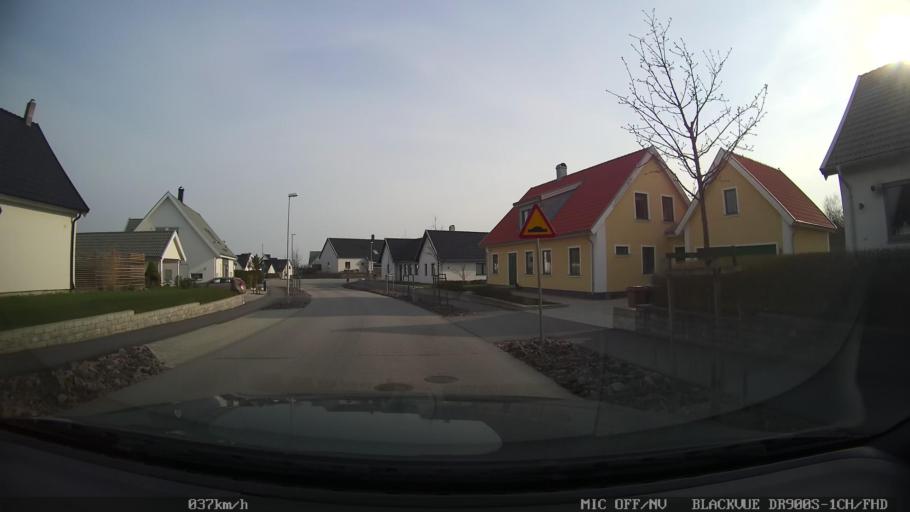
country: SE
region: Skane
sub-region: Ystads Kommun
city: Ystad
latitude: 55.4451
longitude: 13.7947
